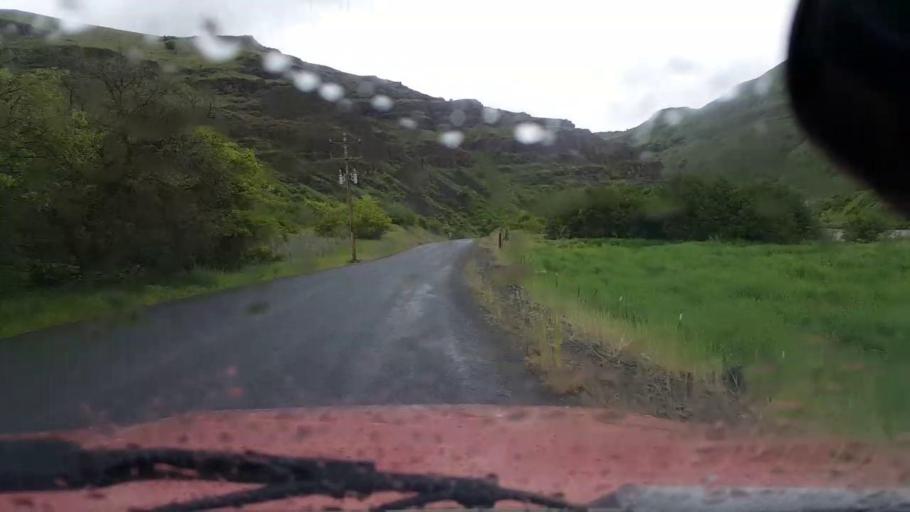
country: US
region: Washington
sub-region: Asotin County
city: Asotin
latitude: 46.0432
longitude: -117.2583
